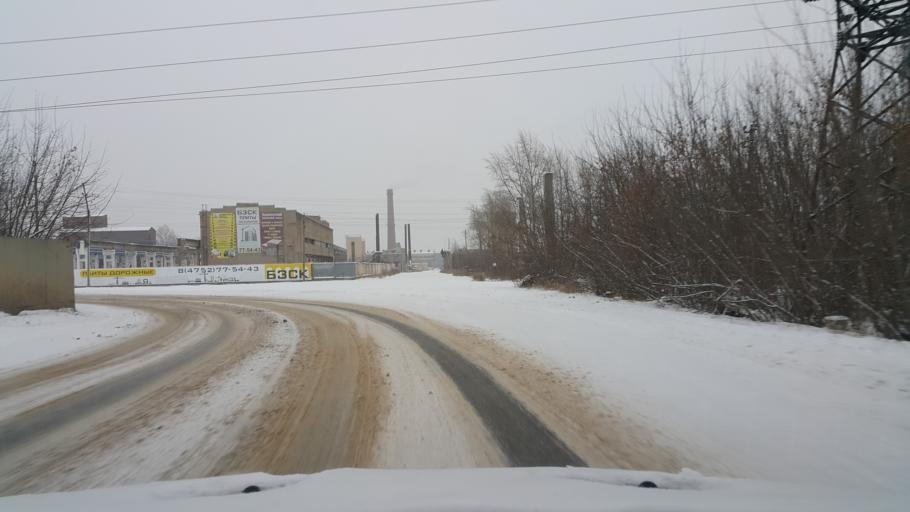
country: RU
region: Tambov
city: Pokrovo-Prigorodnoye
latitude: 52.6545
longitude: 41.4233
